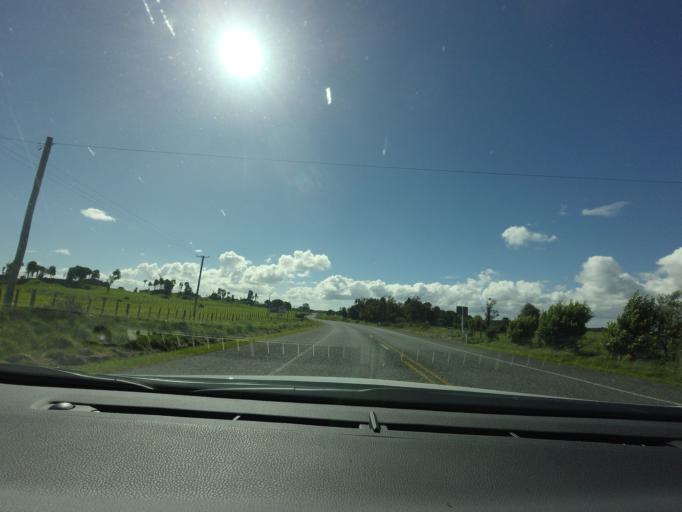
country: NZ
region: Bay of Plenty
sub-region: Rotorua District
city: Rotorua
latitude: -38.0544
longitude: 176.0839
